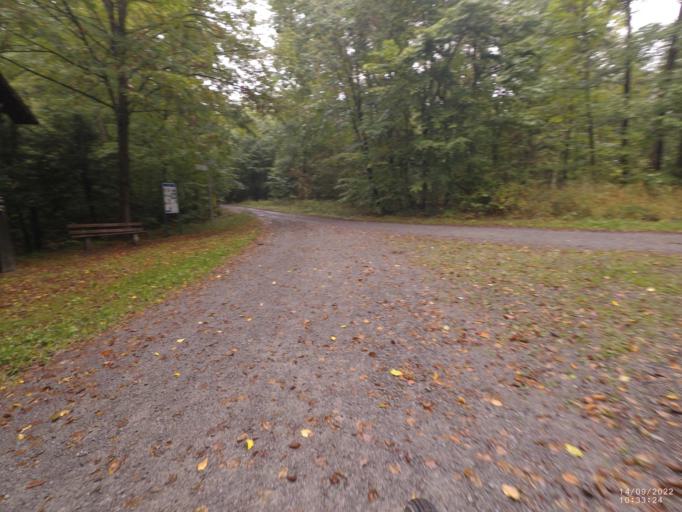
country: DE
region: Bavaria
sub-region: Regierungsbezirk Unterfranken
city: Glattbach
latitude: 50.0173
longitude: 9.1529
